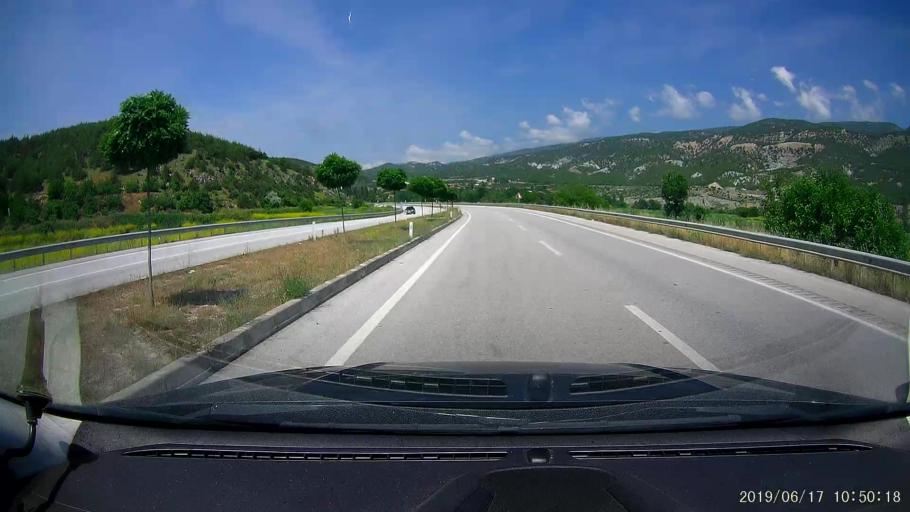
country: TR
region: Corum
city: Hacihamza
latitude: 41.0983
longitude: 34.3882
